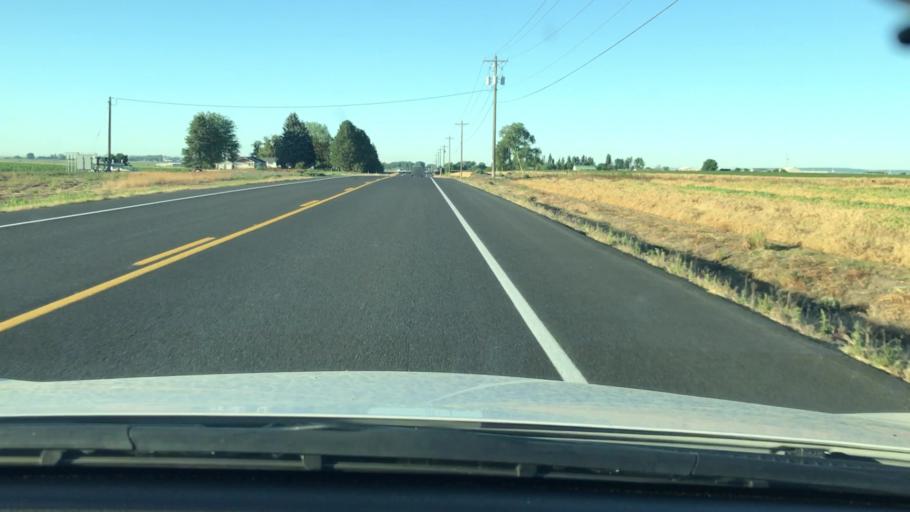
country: US
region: Washington
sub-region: Grant County
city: Moses Lake
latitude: 47.1142
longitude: -119.2360
